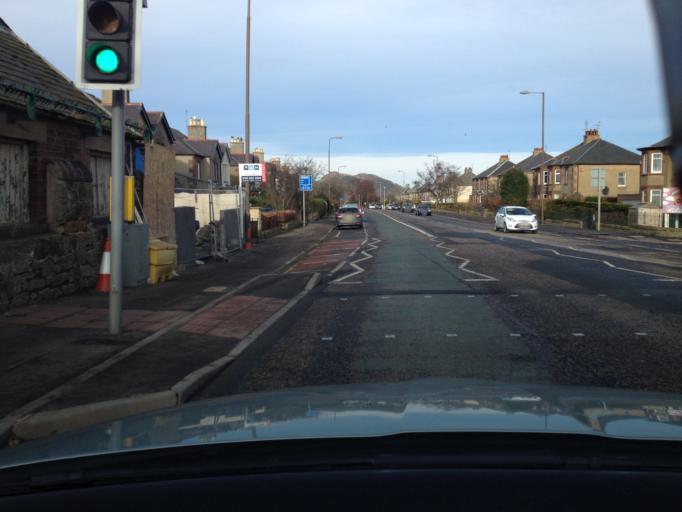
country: GB
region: Scotland
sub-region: Midlothian
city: Loanhead
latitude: 55.9093
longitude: -3.1634
